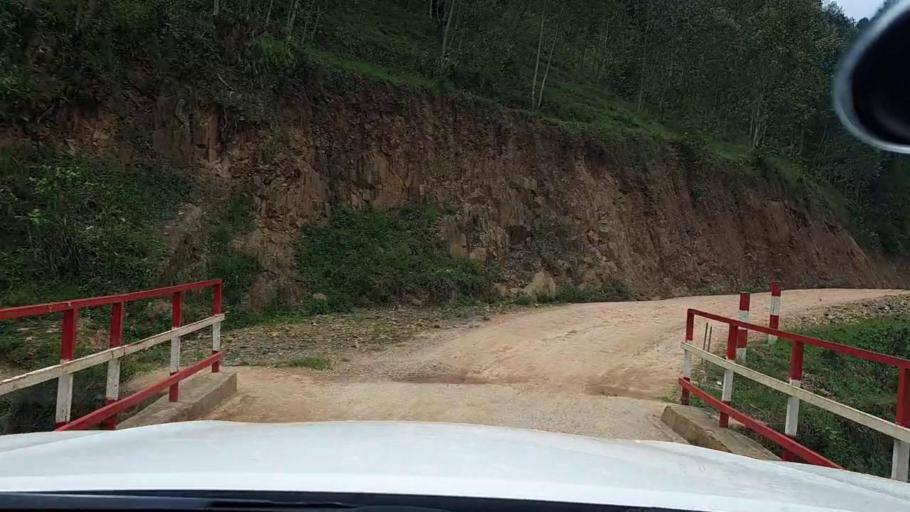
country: RW
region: Western Province
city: Kibuye
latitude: -2.1268
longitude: 29.4266
